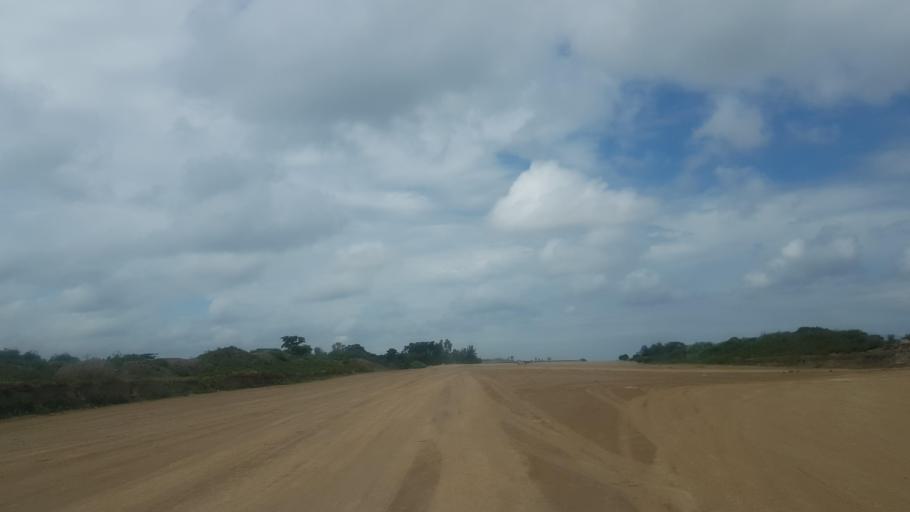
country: ET
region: Oromiya
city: Shashemene
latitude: 7.2473
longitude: 38.5881
